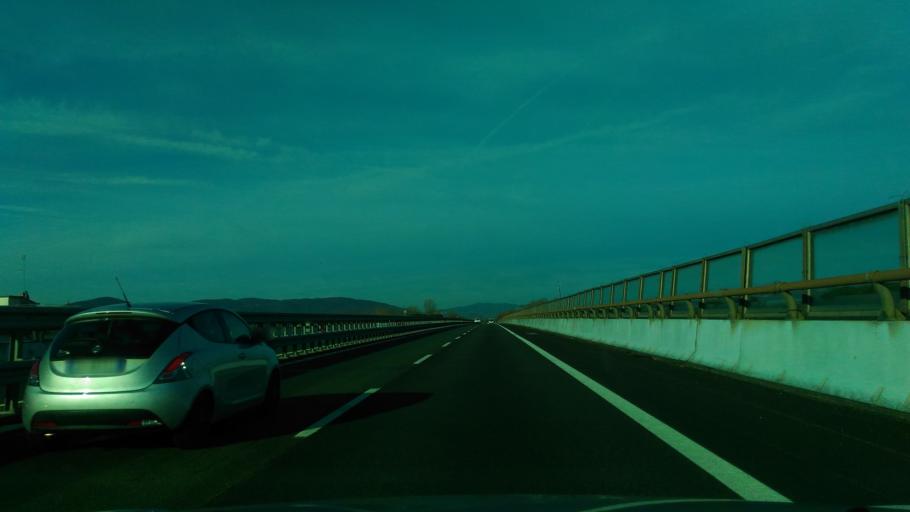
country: IT
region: Tuscany
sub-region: Provincia di Massa-Carrara
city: Marina di Carrara
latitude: 44.0447
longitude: 10.0491
